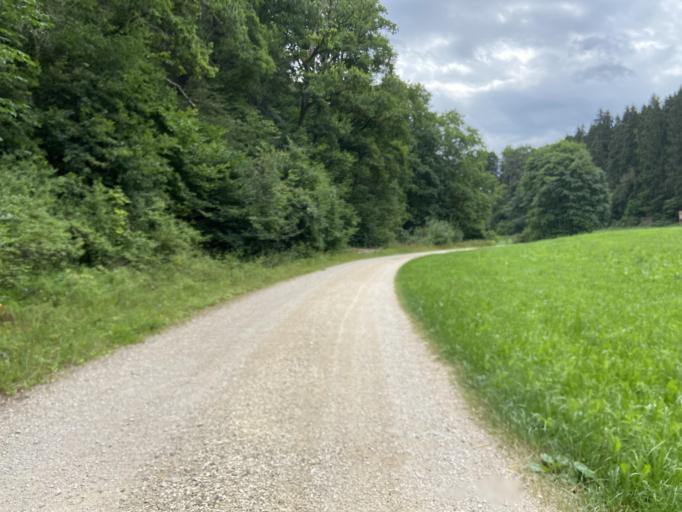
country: DE
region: Baden-Wuerttemberg
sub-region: Tuebingen Region
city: Bingen
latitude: 48.1234
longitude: 9.2750
